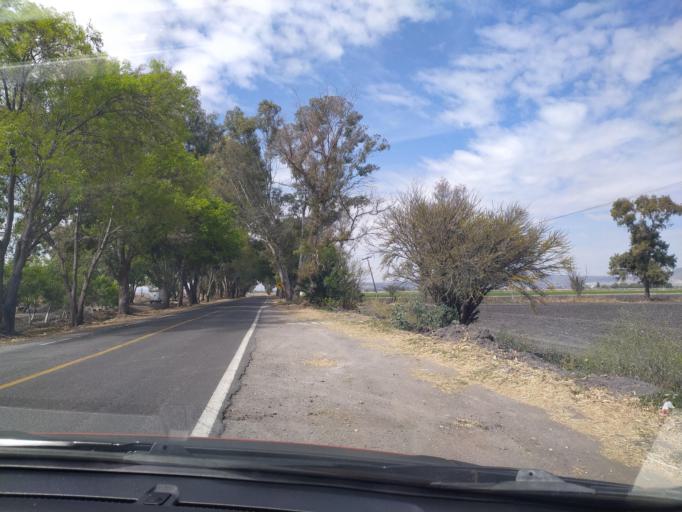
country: MX
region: Guanajuato
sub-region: San Francisco del Rincon
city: San Ignacio de Hidalgo
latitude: 20.8820
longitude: -101.8644
